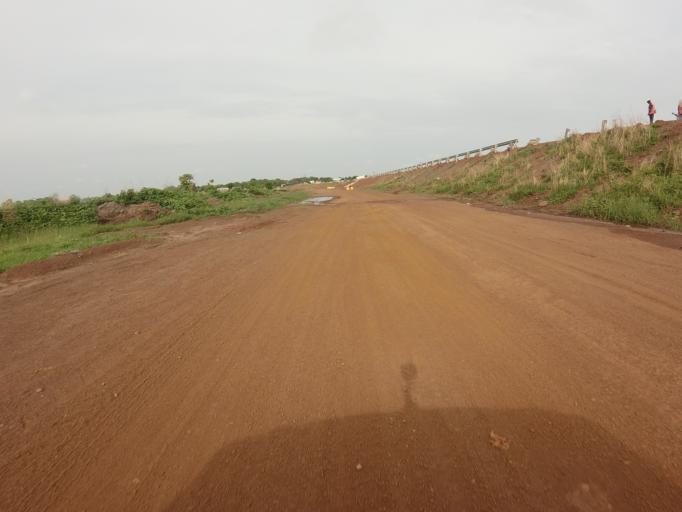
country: GH
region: Northern
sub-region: Yendi
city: Yendi
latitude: 9.9305
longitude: -0.2060
